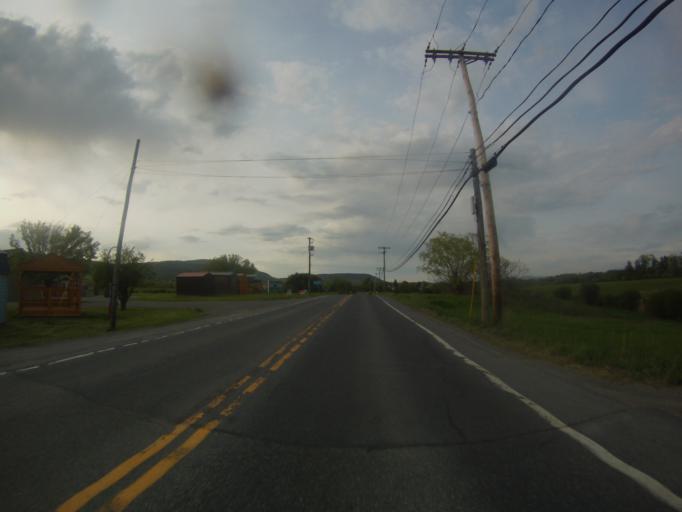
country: US
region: New York
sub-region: Essex County
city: Ticonderoga
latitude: 43.8615
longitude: -73.4378
